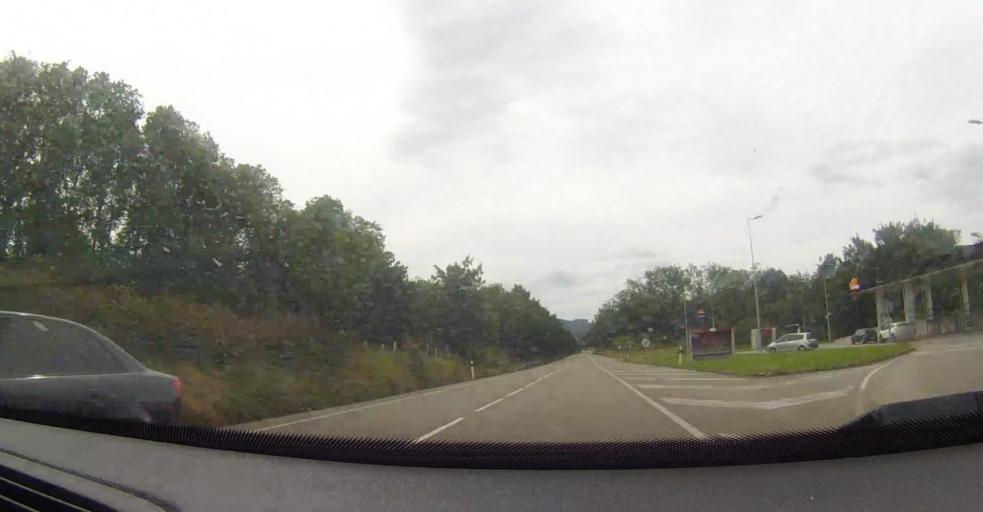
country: ES
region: Asturias
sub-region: Province of Asturias
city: Pilona
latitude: 43.3655
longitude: -5.2711
